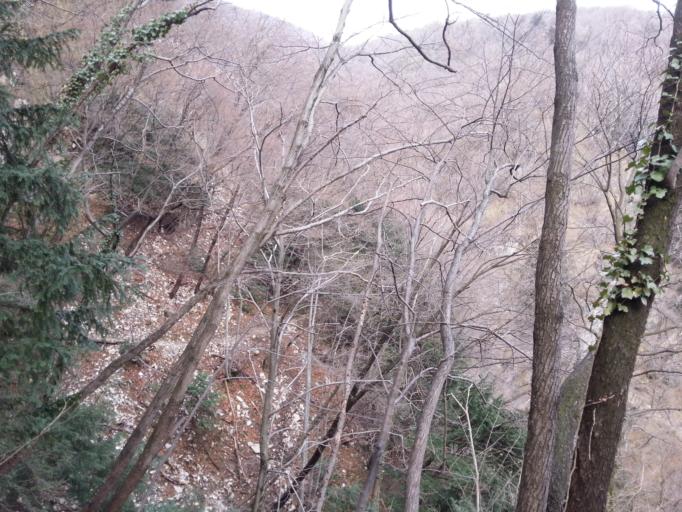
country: CH
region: Ticino
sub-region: Mendrisio District
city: Riva San Vitale
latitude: 45.8939
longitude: 8.9615
